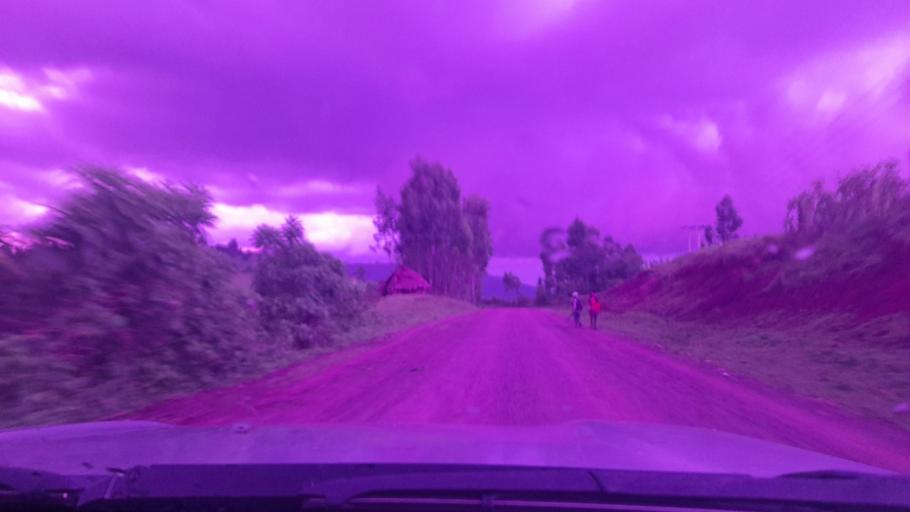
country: ET
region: Southern Nations, Nationalities, and People's Region
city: Mizan Teferi
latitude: 6.9059
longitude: 35.8421
